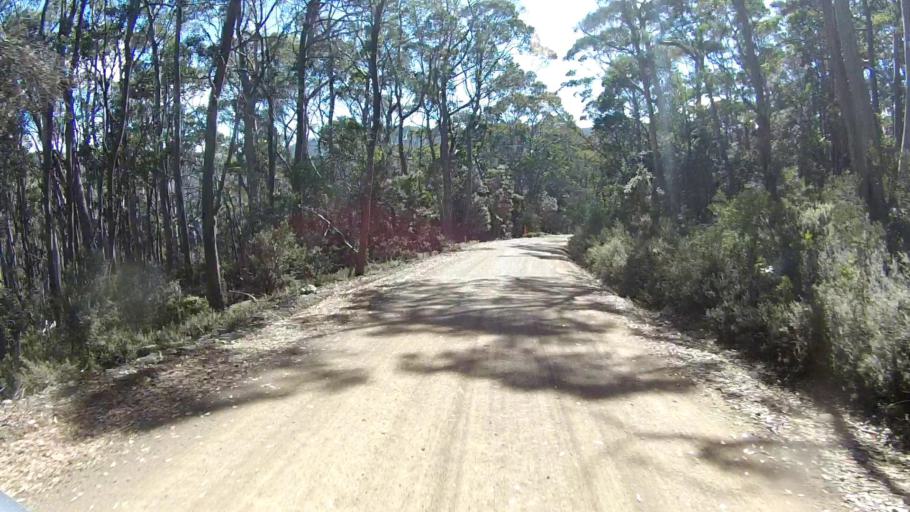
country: AU
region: Tasmania
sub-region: Derwent Valley
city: New Norfolk
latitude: -42.6786
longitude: 146.6207
